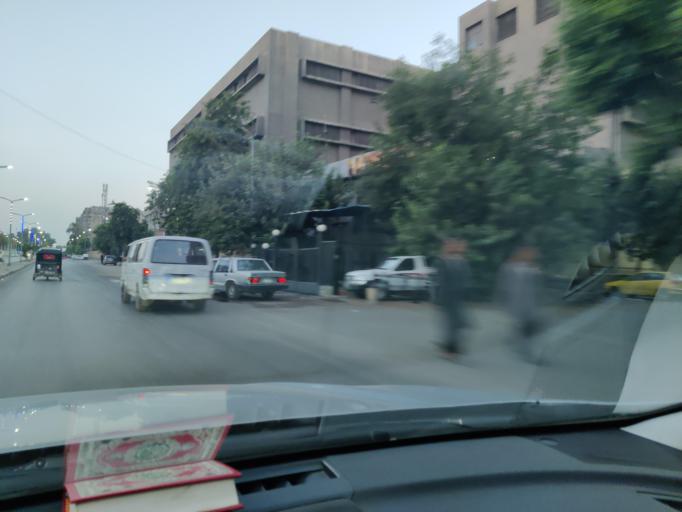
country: EG
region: Muhafazat al Qahirah
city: Cairo
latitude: 30.1065
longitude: 31.3028
